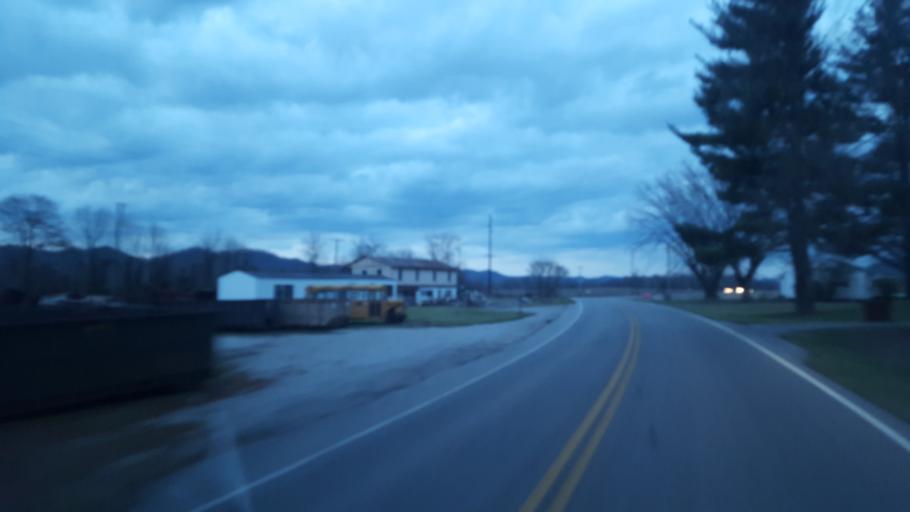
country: US
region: Ohio
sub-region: Scioto County
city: West Portsmouth
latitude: 38.6263
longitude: -83.1284
